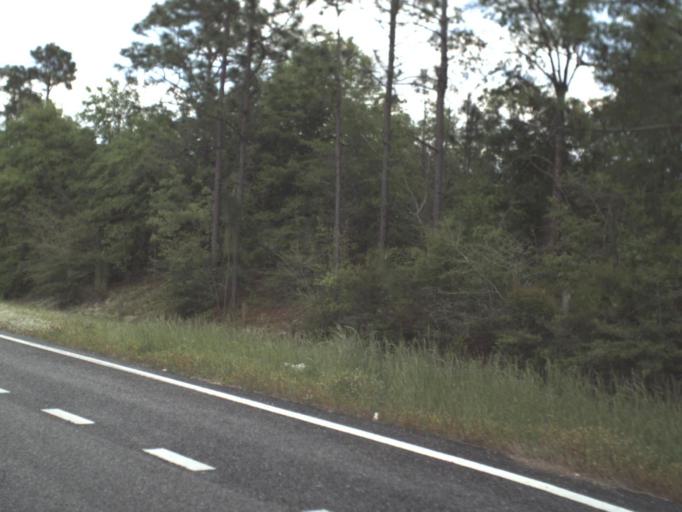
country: US
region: Florida
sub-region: Escambia County
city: Molino
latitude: 30.7604
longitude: -87.3421
